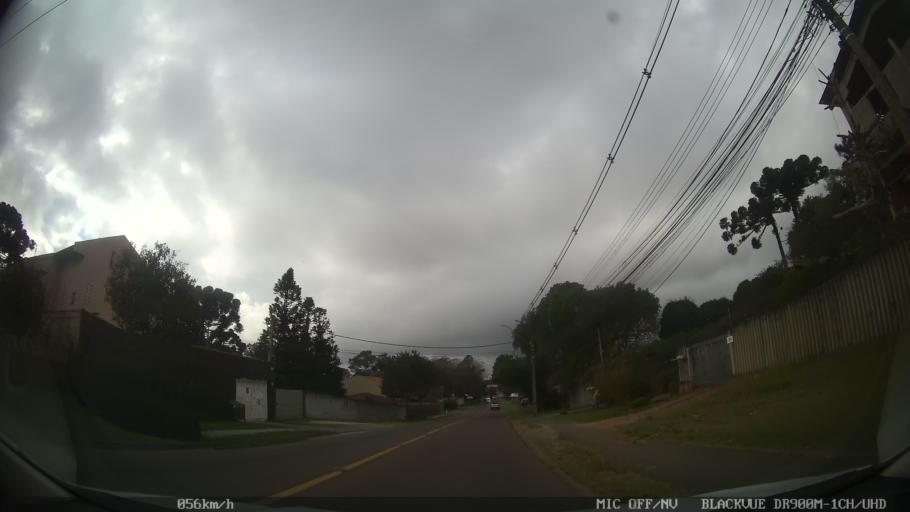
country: BR
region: Parana
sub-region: Curitiba
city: Curitiba
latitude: -25.3714
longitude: -49.2310
